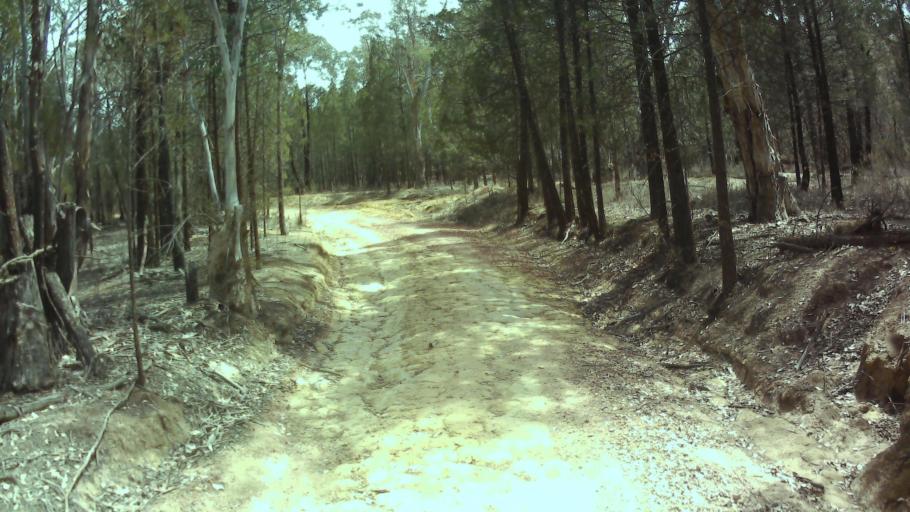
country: AU
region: New South Wales
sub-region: Weddin
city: Grenfell
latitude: -33.8861
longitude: 148.3829
